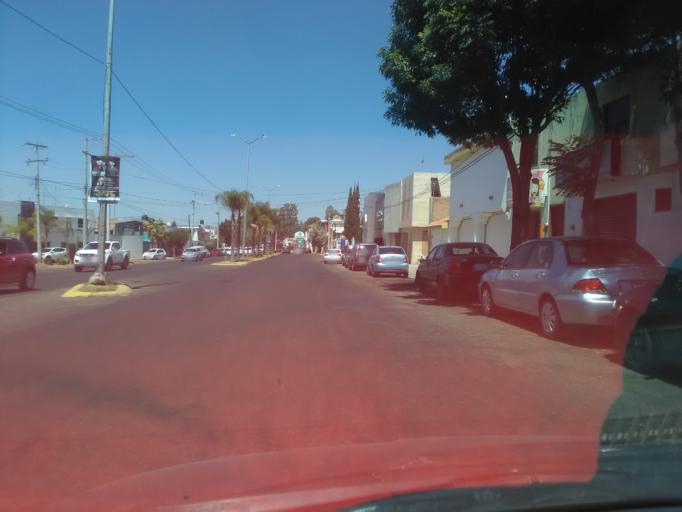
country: MX
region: Durango
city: Victoria de Durango
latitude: 24.0138
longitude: -104.6796
